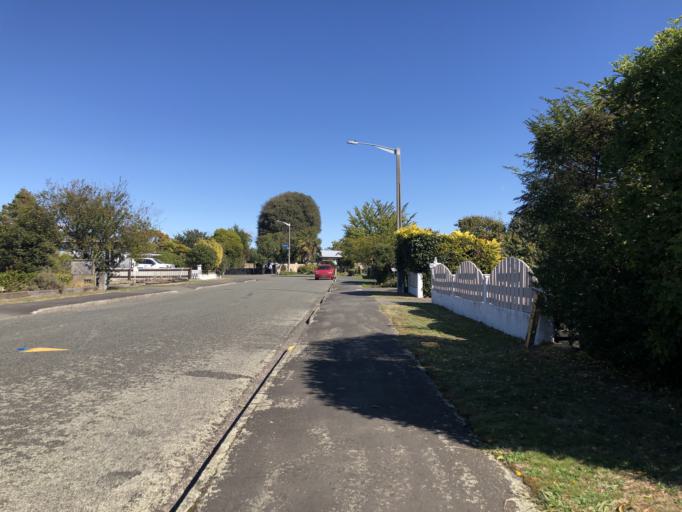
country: NZ
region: Tasman
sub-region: Tasman District
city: Richmond
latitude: -41.3417
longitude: 173.1756
